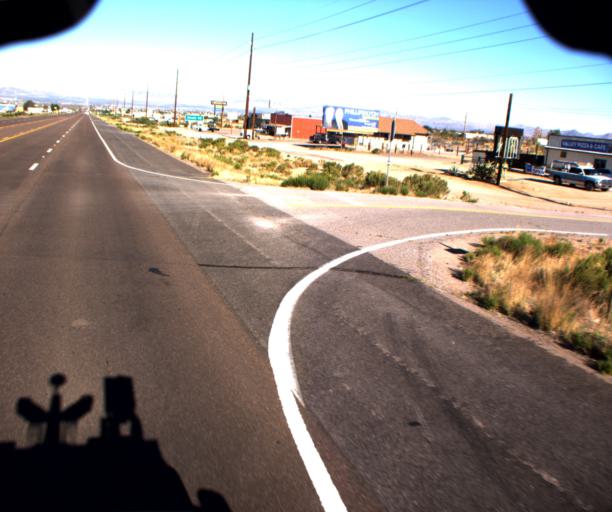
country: US
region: Arizona
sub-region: Mohave County
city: Golden Valley
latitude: 35.2197
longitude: -114.1674
